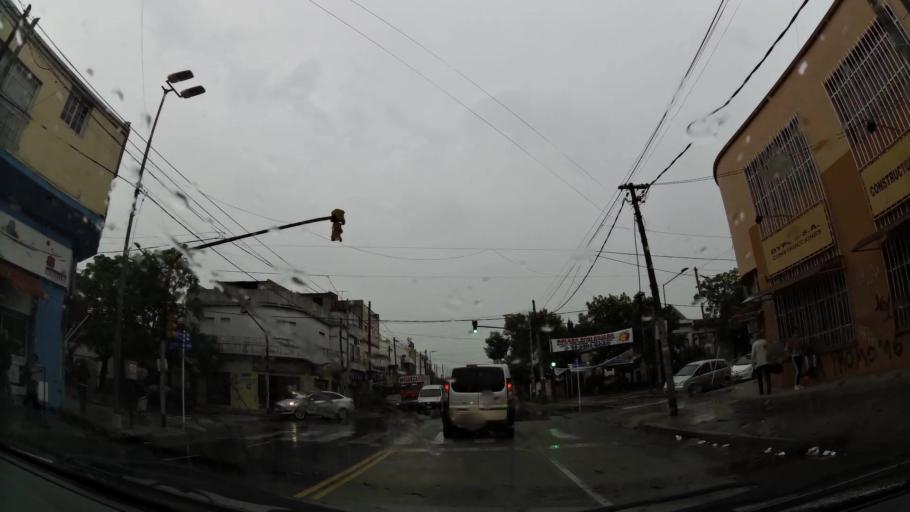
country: AR
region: Buenos Aires
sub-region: Partido de Lanus
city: Lanus
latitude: -34.7067
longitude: -58.4019
